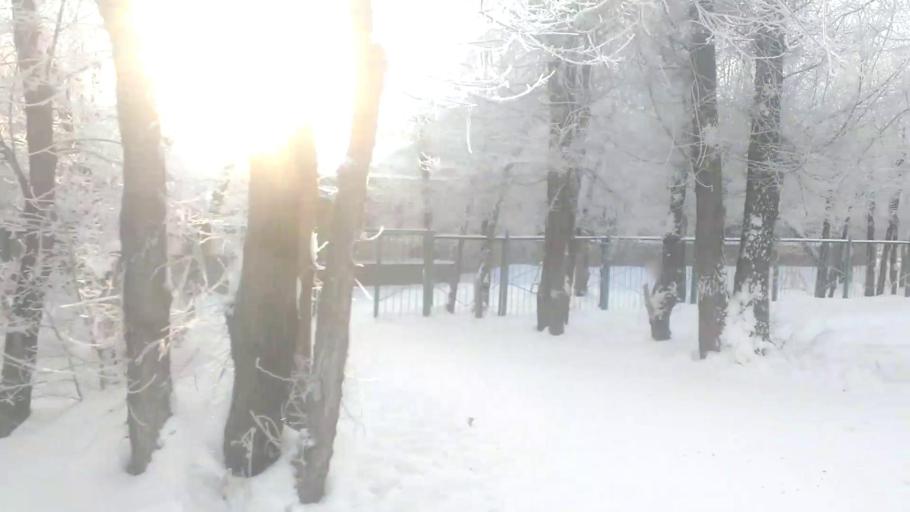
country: RU
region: Altai Krai
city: Novosilikatnyy
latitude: 53.3759
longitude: 83.6741
